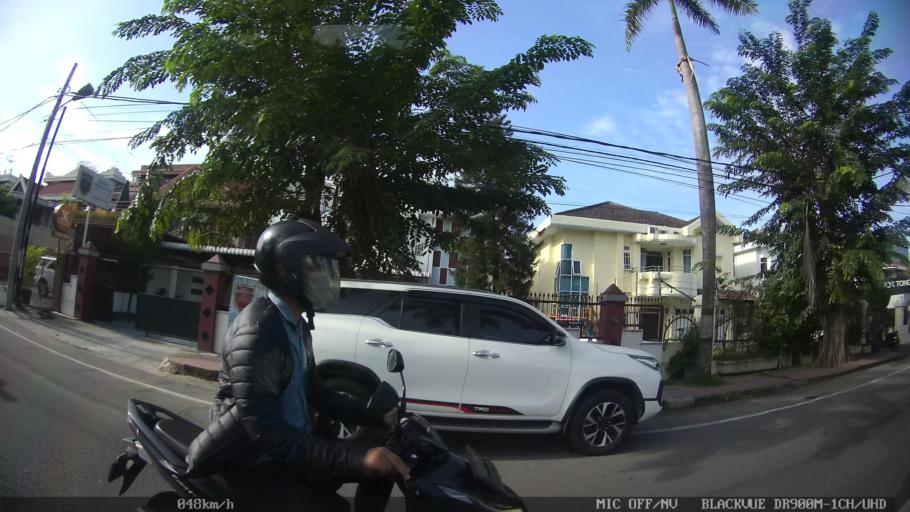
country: ID
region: North Sumatra
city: Medan
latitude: 3.6079
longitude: 98.6498
